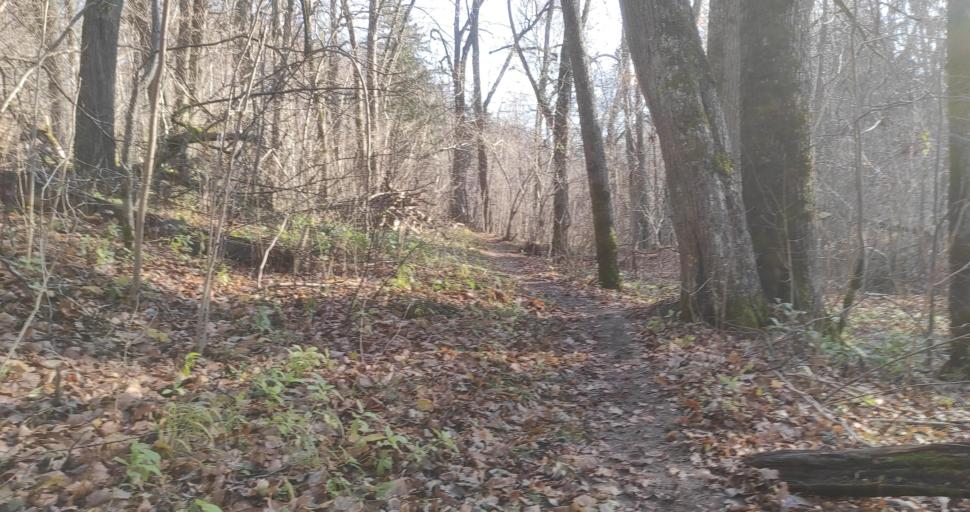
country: LV
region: Saldus Rajons
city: Saldus
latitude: 56.6651
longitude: 22.5187
